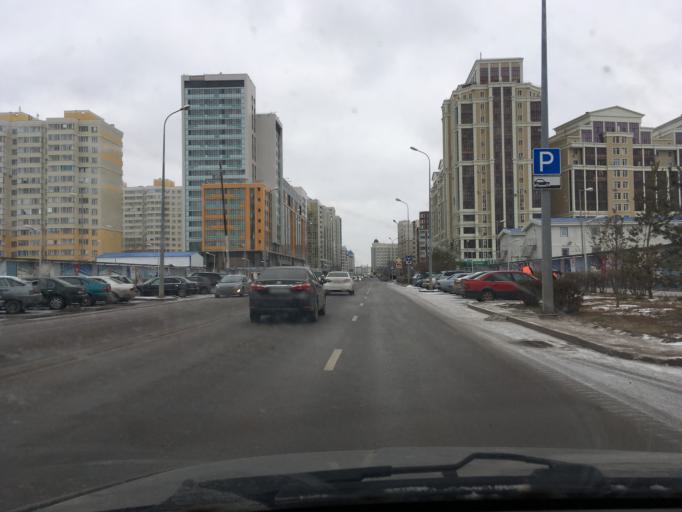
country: KZ
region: Astana Qalasy
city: Astana
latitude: 51.1164
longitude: 71.4257
